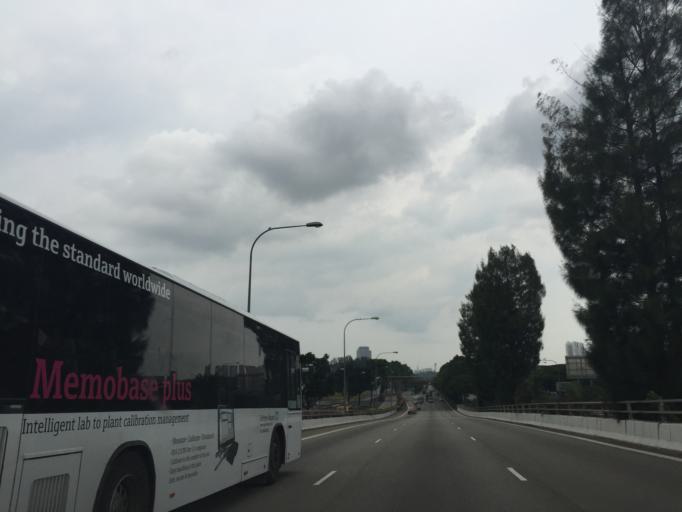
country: SG
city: Singapore
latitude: 1.3239
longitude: 103.7207
